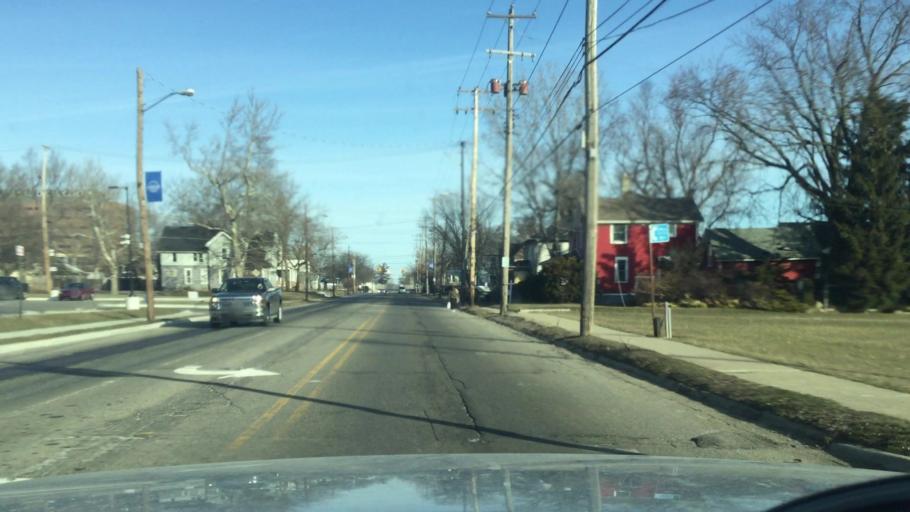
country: US
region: Michigan
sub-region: Genesee County
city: Flint
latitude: 43.0192
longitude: -83.6998
